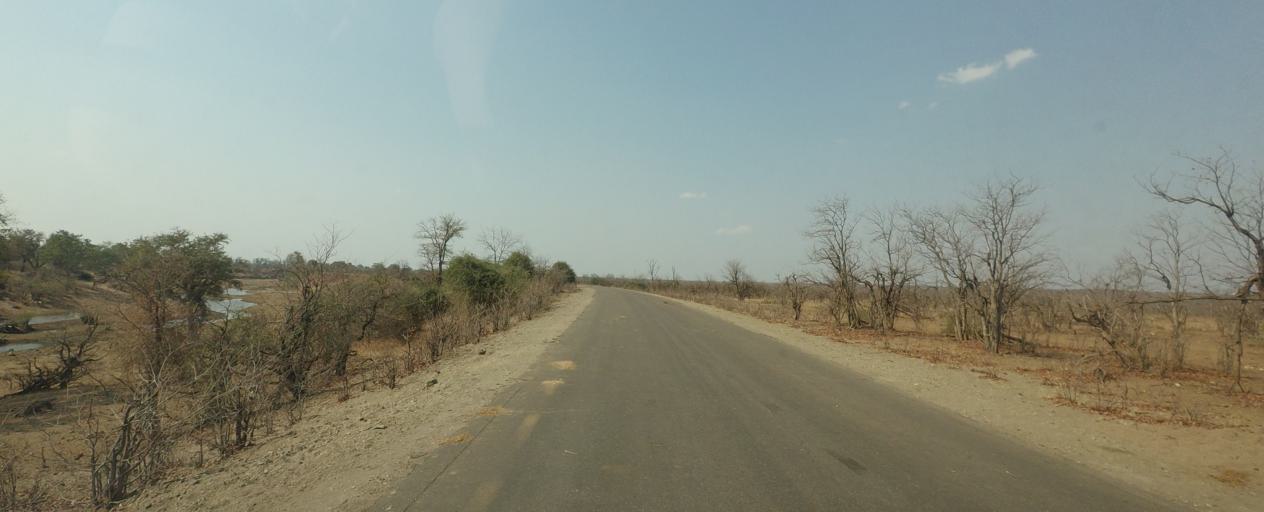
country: ZA
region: Limpopo
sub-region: Mopani District Municipality
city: Giyani
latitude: -23.1376
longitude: 31.3764
